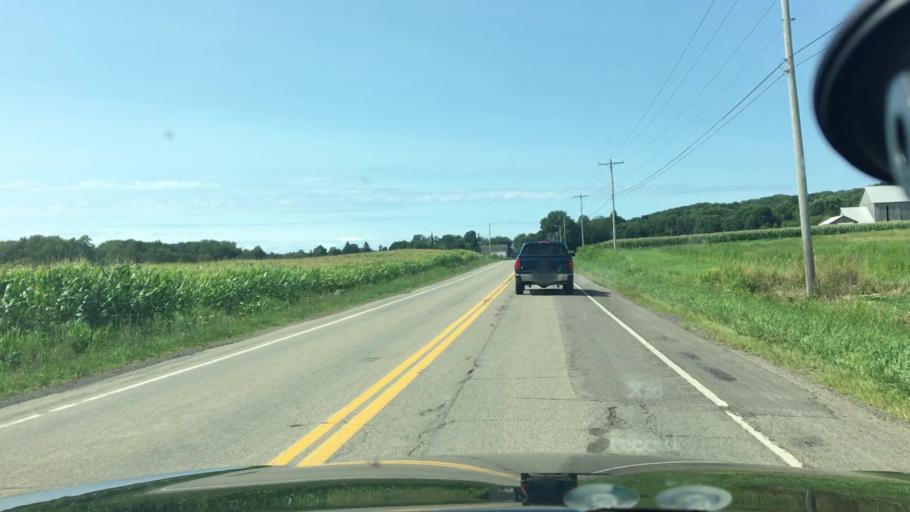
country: US
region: New York
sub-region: Chautauqua County
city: Brocton
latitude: 42.3107
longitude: -79.3538
